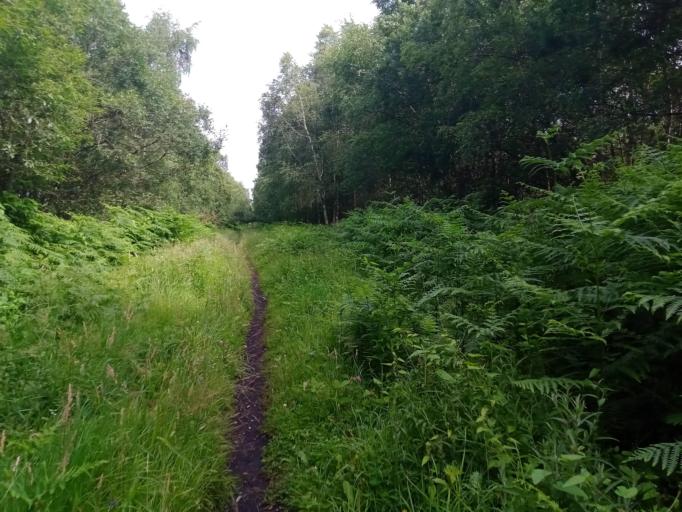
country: IE
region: Leinster
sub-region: Laois
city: Abbeyleix
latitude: 52.8850
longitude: -7.3504
